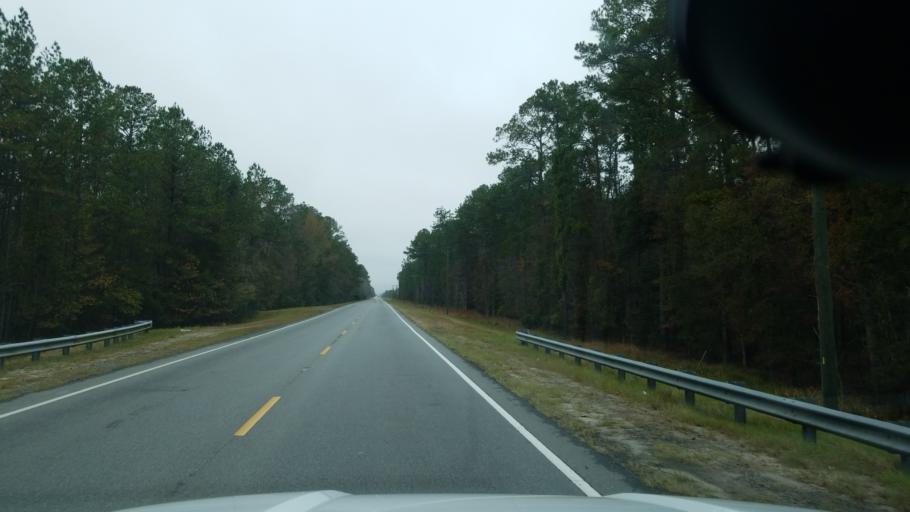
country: US
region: Georgia
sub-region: Charlton County
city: Folkston
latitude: 30.8331
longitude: -81.8820
